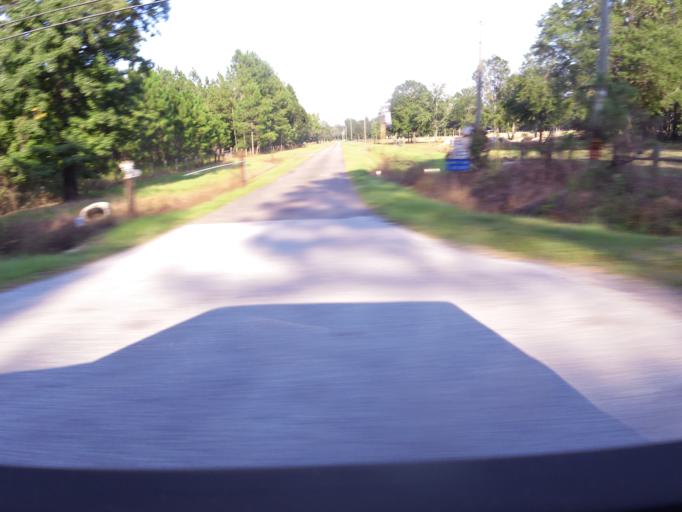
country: US
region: Florida
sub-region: Duval County
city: Baldwin
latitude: 30.3081
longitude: -82.0084
